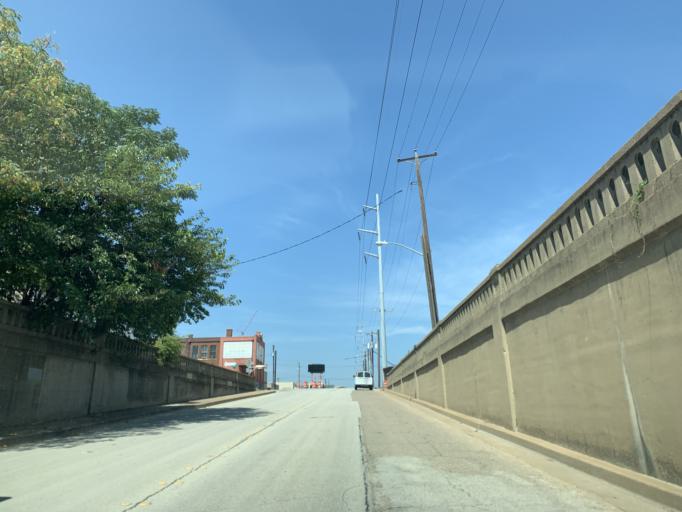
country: US
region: Texas
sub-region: Tarrant County
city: Fort Worth
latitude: 32.7435
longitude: -97.3219
